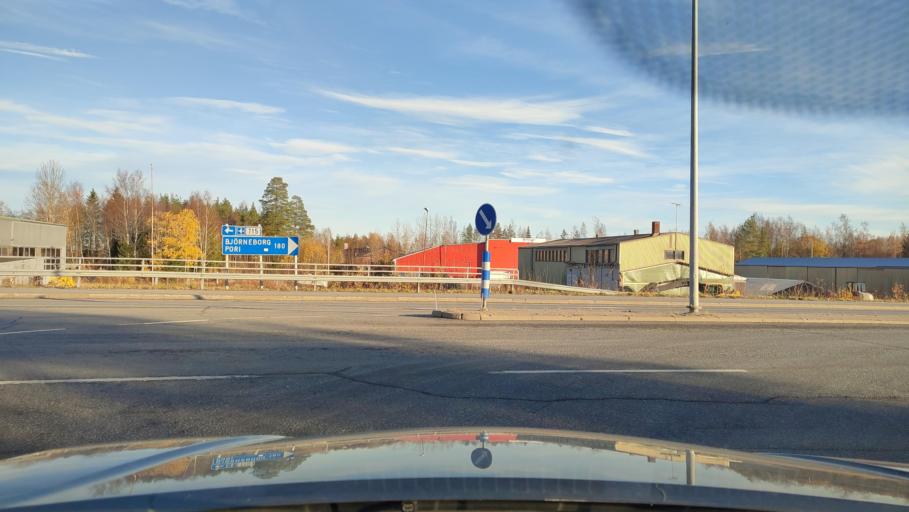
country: FI
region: Ostrobothnia
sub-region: Vaasa
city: Ristinummi
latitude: 63.0275
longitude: 21.7562
